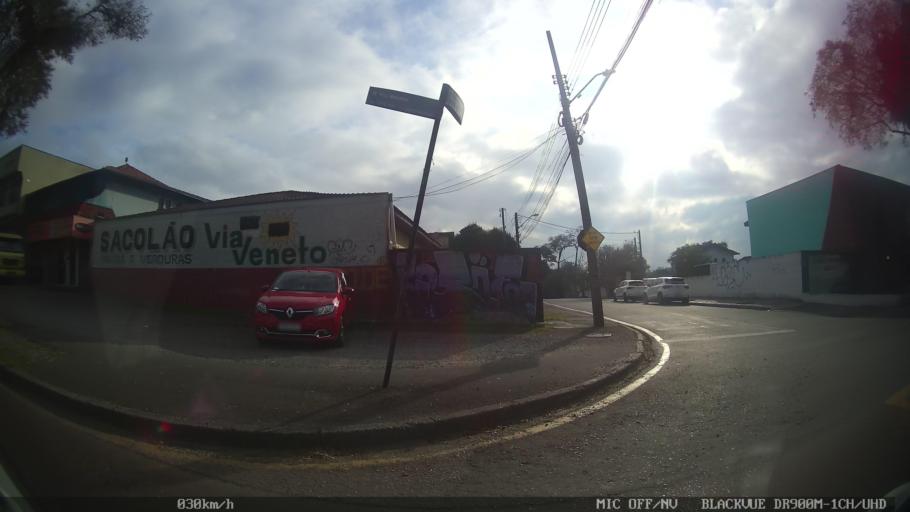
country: BR
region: Parana
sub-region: Curitiba
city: Curitiba
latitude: -25.3998
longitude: -49.3334
